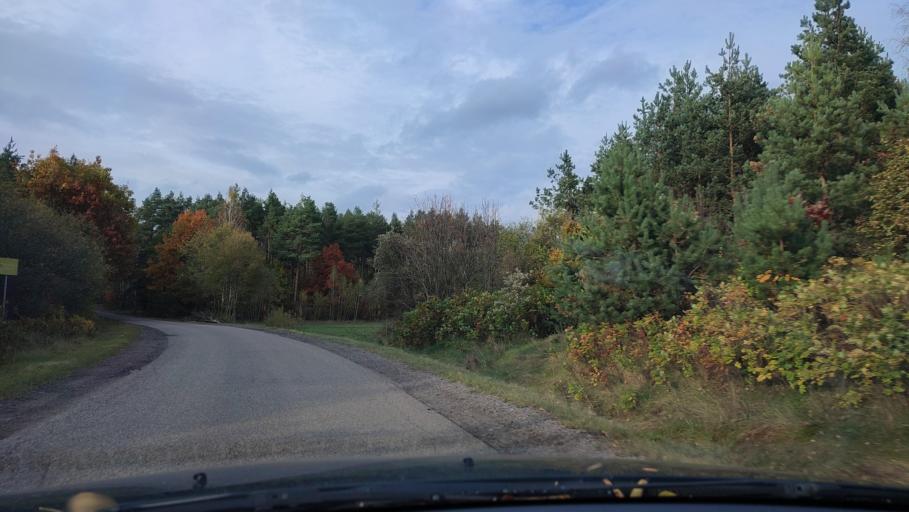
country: PL
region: Masovian Voivodeship
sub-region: Powiat mlawski
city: Mlawa
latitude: 53.1427
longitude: 20.3704
